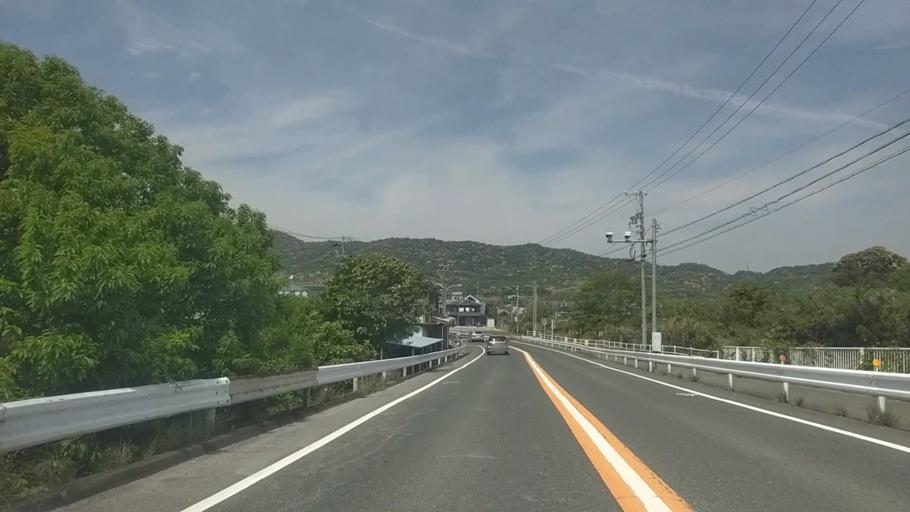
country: JP
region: Shizuoka
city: Kosai-shi
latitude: 34.7508
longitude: 137.5115
